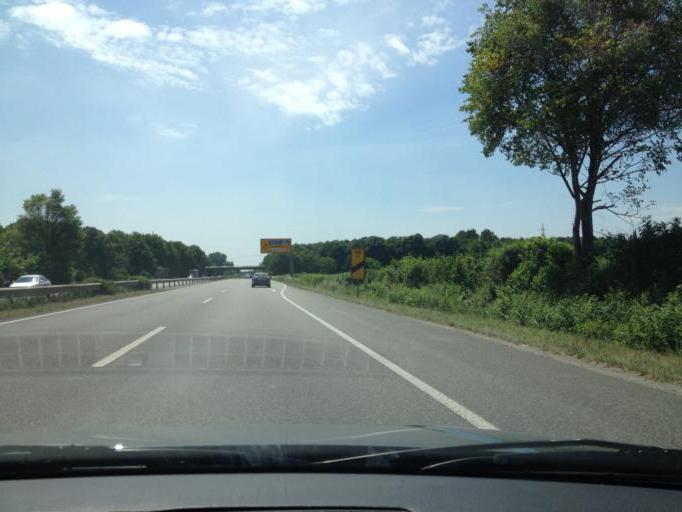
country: DE
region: Rheinland-Pfalz
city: Limburgerhof
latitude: 49.4384
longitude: 8.4067
